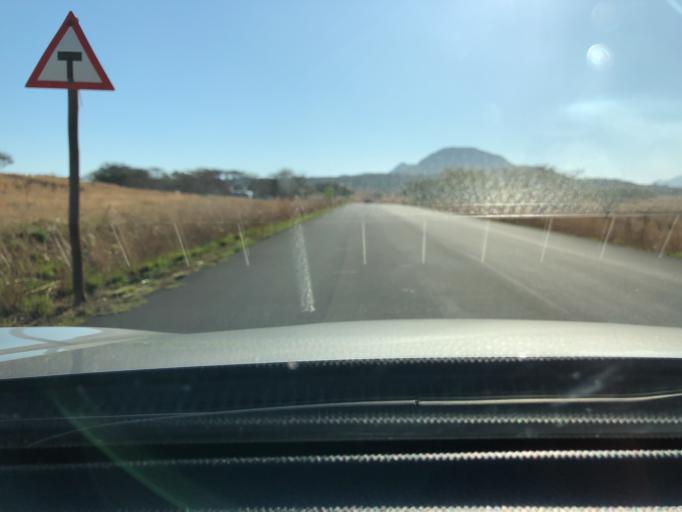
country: ZA
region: KwaZulu-Natal
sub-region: uThukela District Municipality
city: Ladysmith
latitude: -28.4010
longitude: 29.9346
